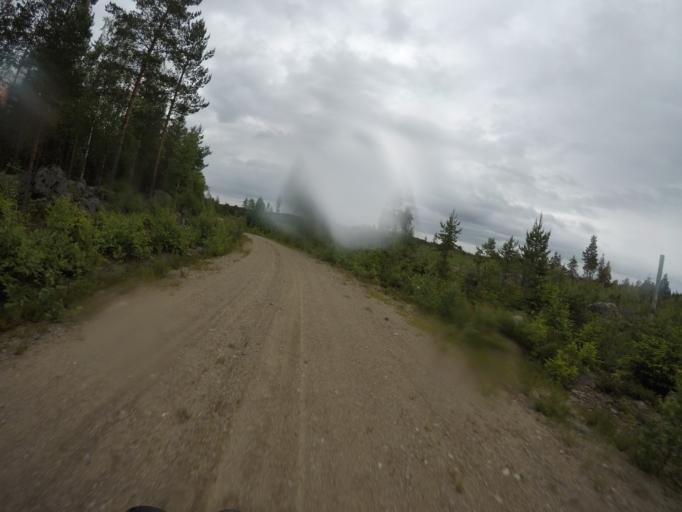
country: SE
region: Dalarna
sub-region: Ludvika Kommun
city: Abborrberget
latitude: 60.0525
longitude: 14.5766
